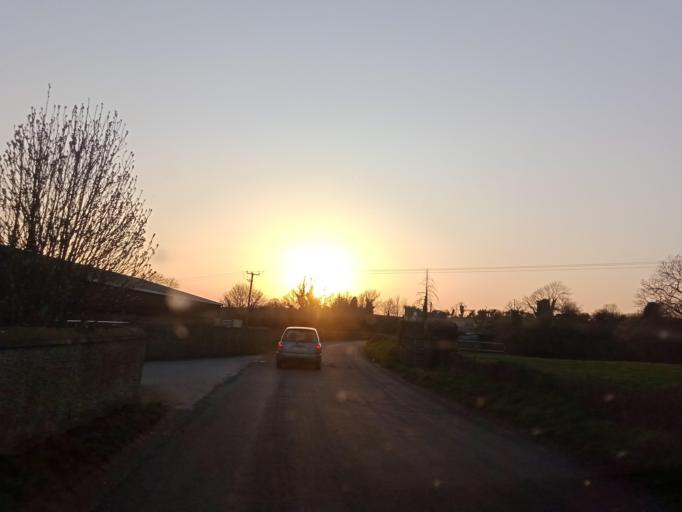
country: IE
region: Leinster
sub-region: Laois
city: Abbeyleix
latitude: 52.8658
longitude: -7.2955
